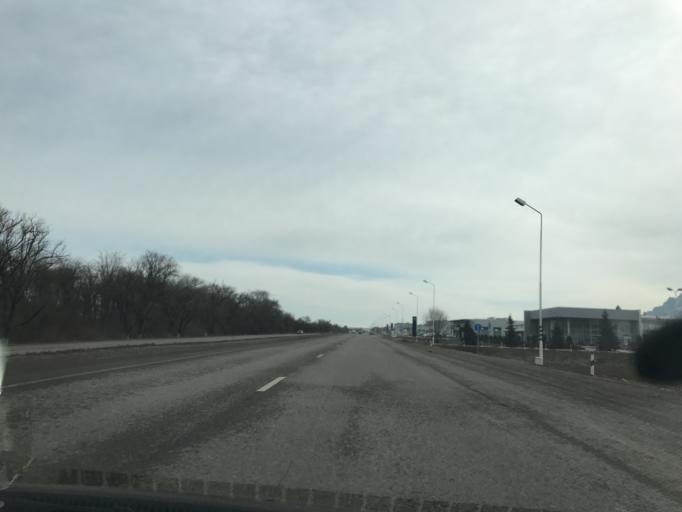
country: RU
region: Stavropol'skiy
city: Andzhiyevskiy
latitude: 44.2244
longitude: 43.0576
